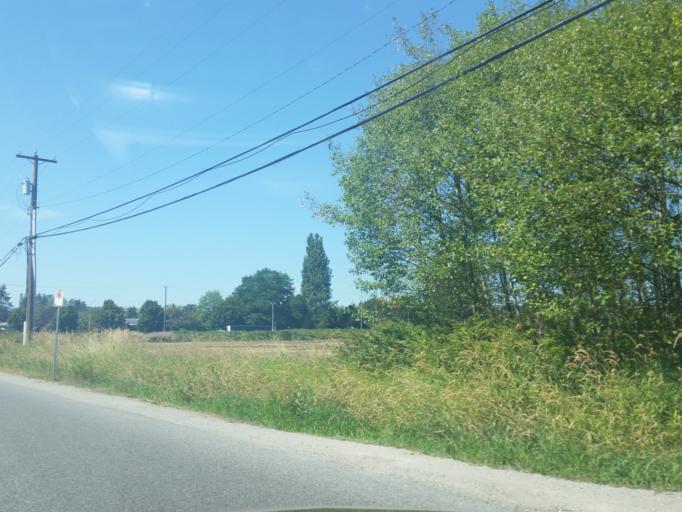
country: CA
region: British Columbia
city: Langley
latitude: 49.1226
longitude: -122.6658
